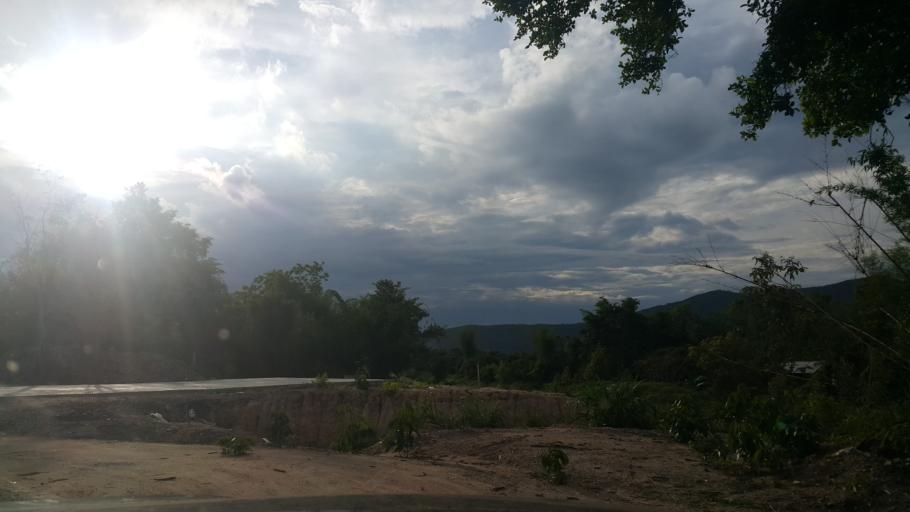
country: TH
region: Chiang Mai
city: Mae On
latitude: 18.7245
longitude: 99.2210
